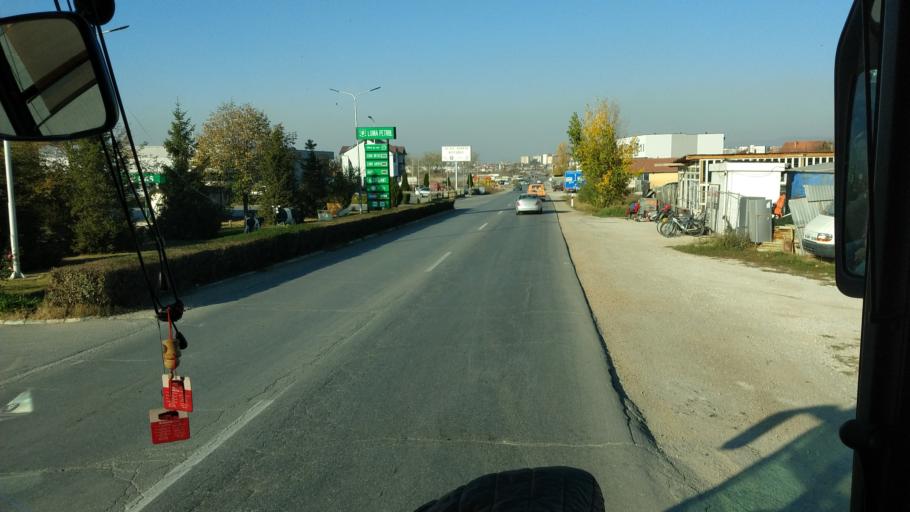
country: XK
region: Pristina
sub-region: Lipjan
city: Lipljan
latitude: 42.5078
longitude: 21.1116
